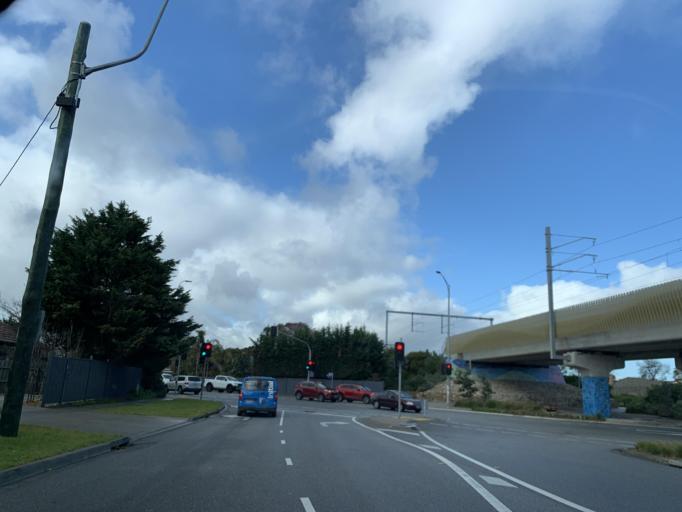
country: AU
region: Victoria
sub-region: Frankston
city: Seaford
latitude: -38.1101
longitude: 145.1305
